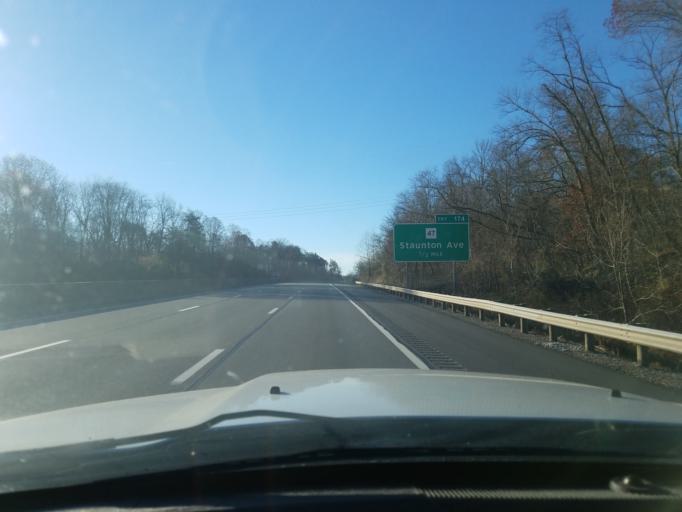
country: US
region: West Virginia
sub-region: Wood County
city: Mineral Wells
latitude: 39.2438
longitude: -81.5004
